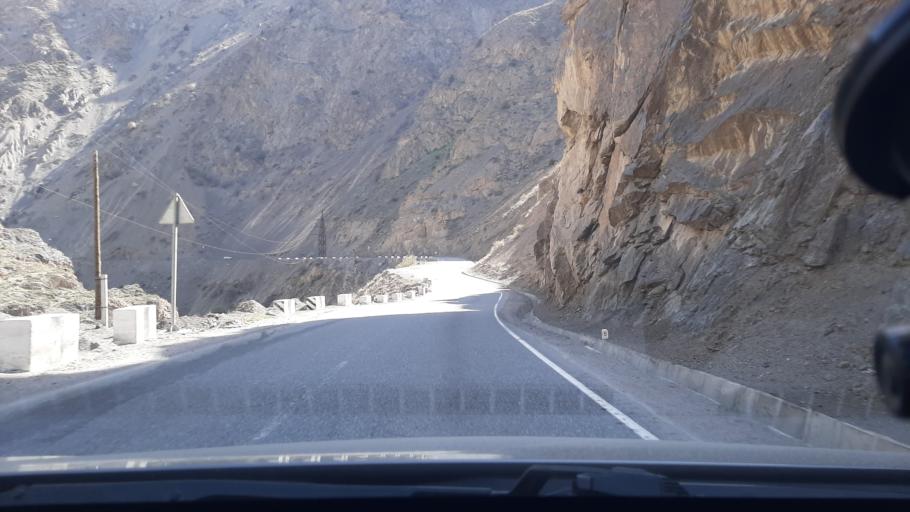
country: TJ
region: Viloyati Sughd
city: Ayni
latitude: 39.3315
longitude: 68.5503
